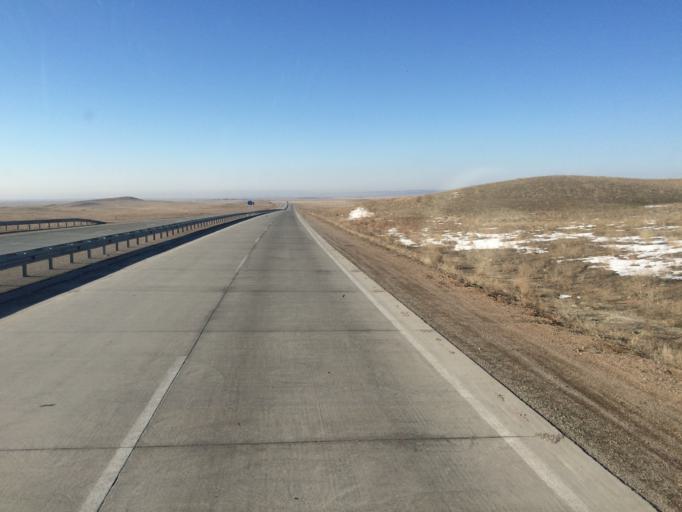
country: KZ
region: Zhambyl
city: Georgiyevka
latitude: 43.3393
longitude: 74.4620
